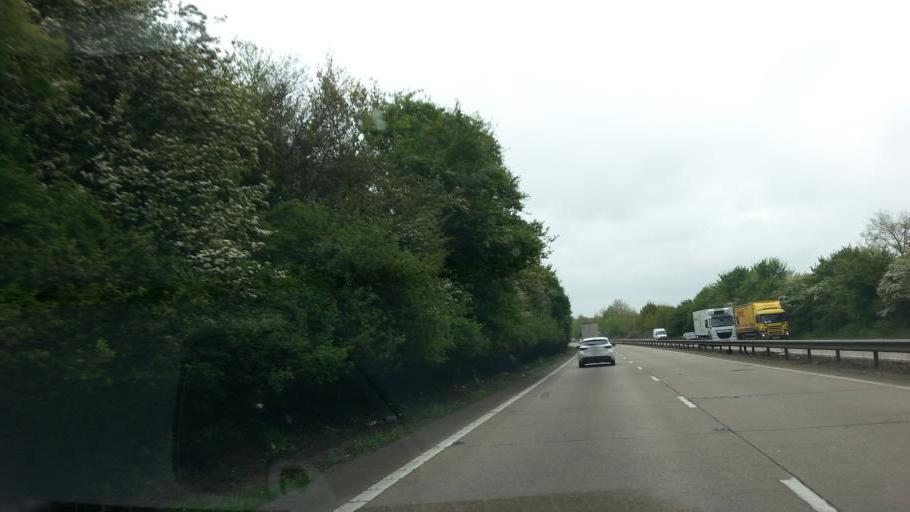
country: GB
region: England
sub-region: Suffolk
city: Elmswell
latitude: 52.2162
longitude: 0.9374
